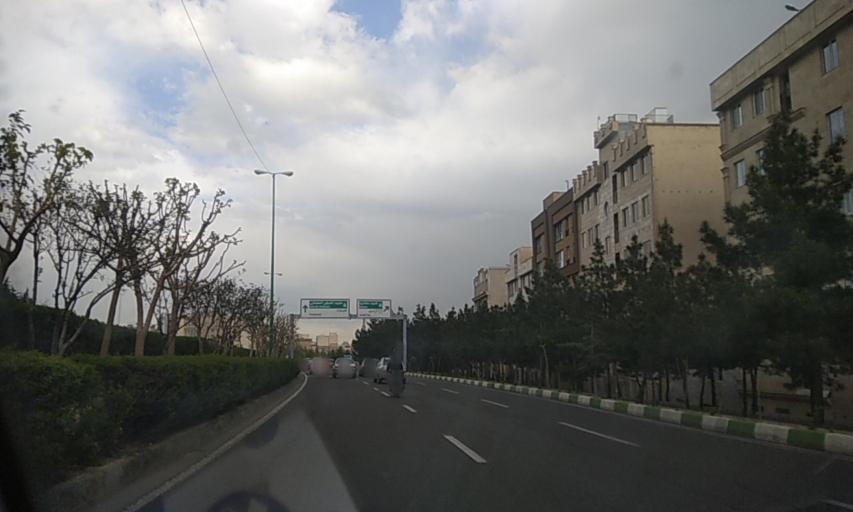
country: IR
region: Tehran
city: Tajrish
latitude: 35.7778
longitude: 51.3170
